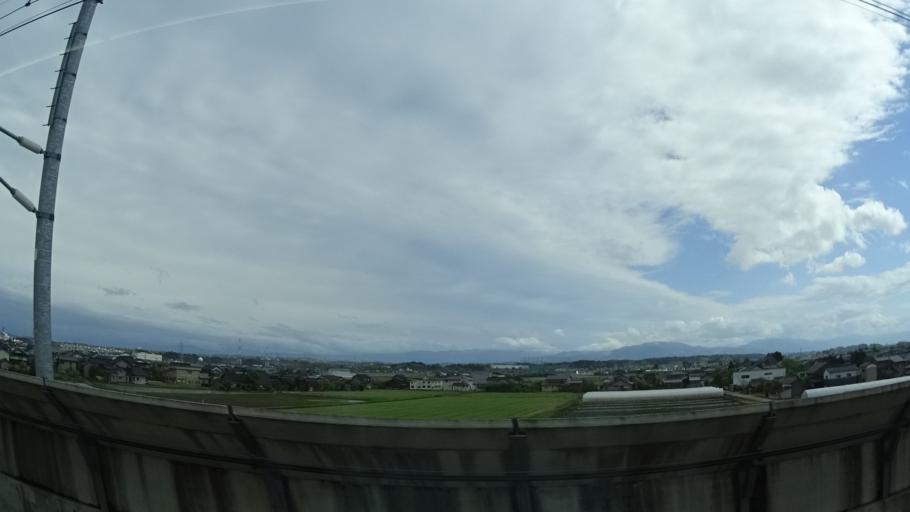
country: JP
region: Toyama
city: Takaoka
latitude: 36.7210
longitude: 137.0622
